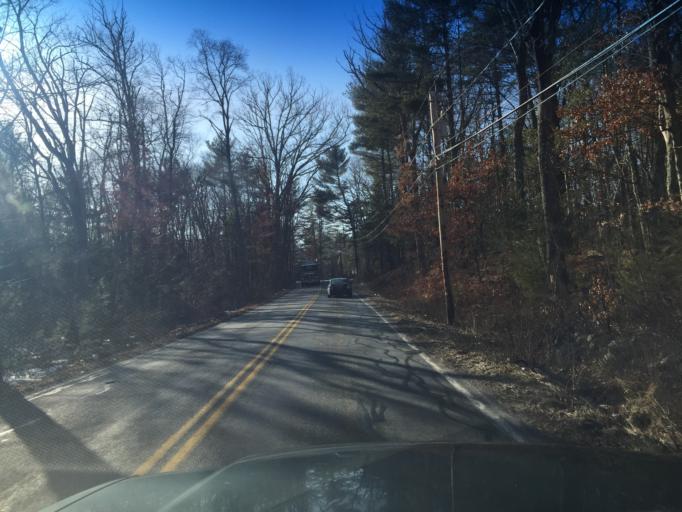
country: US
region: Massachusetts
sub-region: Norfolk County
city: Bellingham
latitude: 42.0893
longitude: -71.5051
